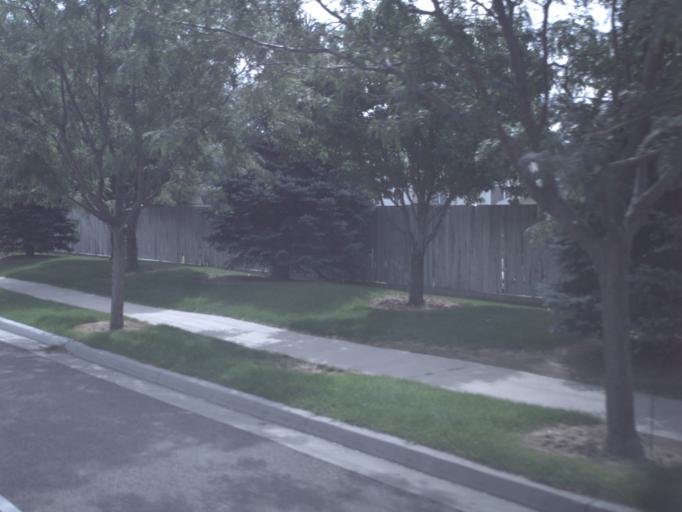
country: US
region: Utah
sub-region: Utah County
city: Alpine
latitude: 40.4318
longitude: -111.7982
